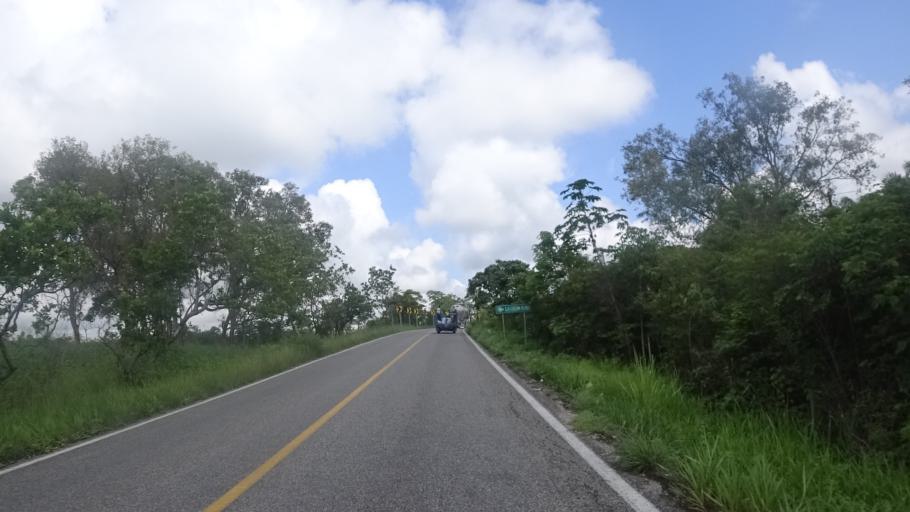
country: MX
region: Chiapas
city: Palenque
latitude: 17.5874
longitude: -92.0344
